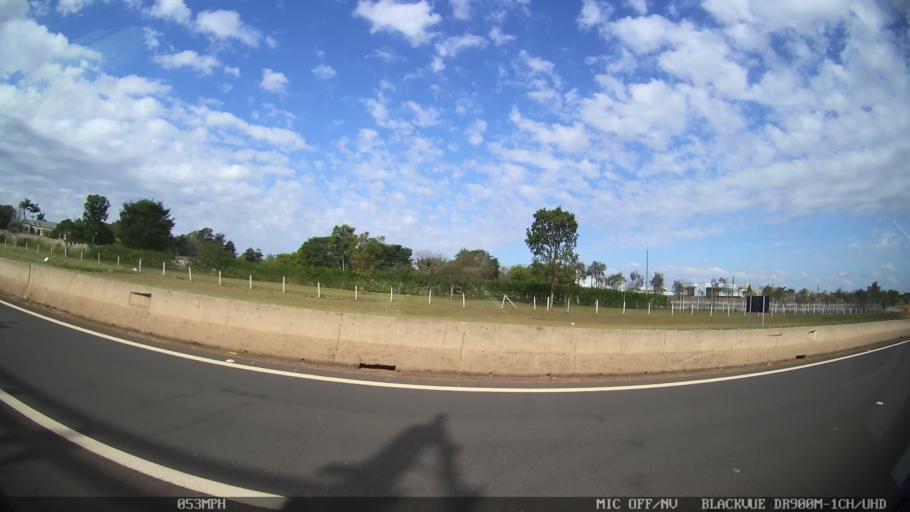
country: BR
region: Sao Paulo
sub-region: Limeira
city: Limeira
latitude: -22.5742
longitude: -47.4481
